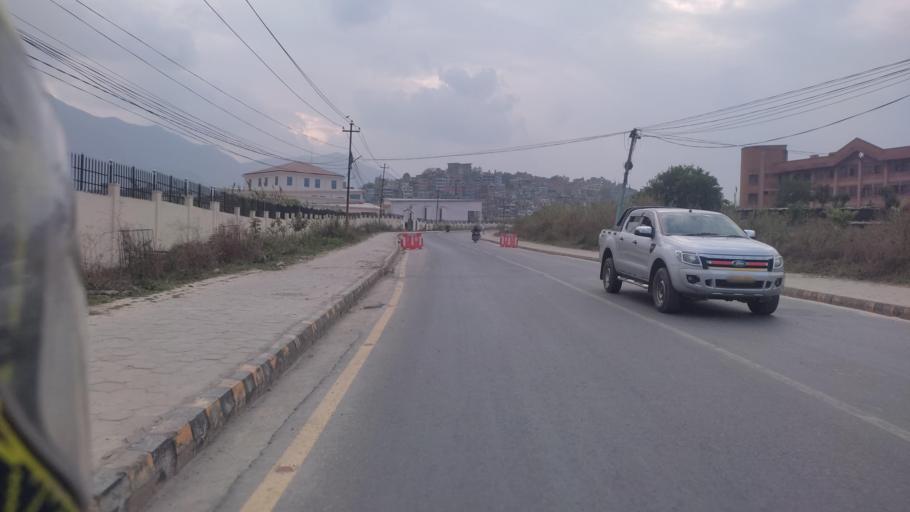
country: NP
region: Central Region
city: Kirtipur
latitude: 27.6759
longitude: 85.2863
